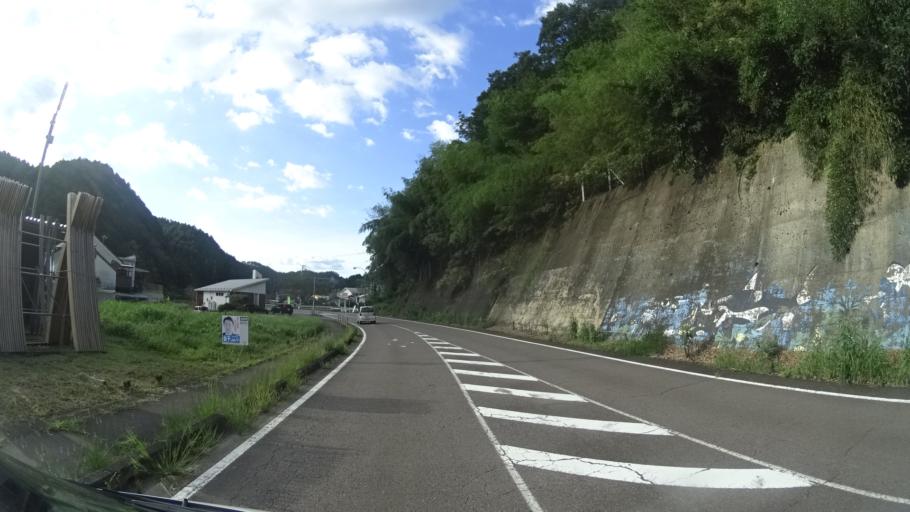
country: JP
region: Gifu
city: Minokamo
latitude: 35.5778
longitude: 137.0901
